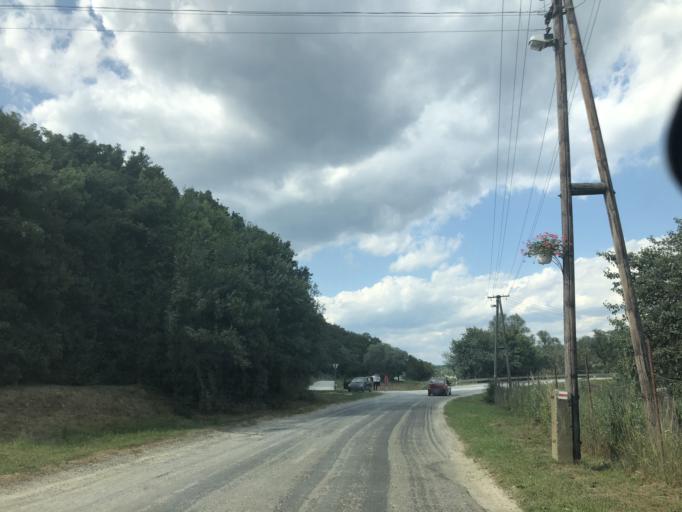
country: HU
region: Borsod-Abauj-Zemplen
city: Szendro
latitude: 48.4419
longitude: 20.7932
